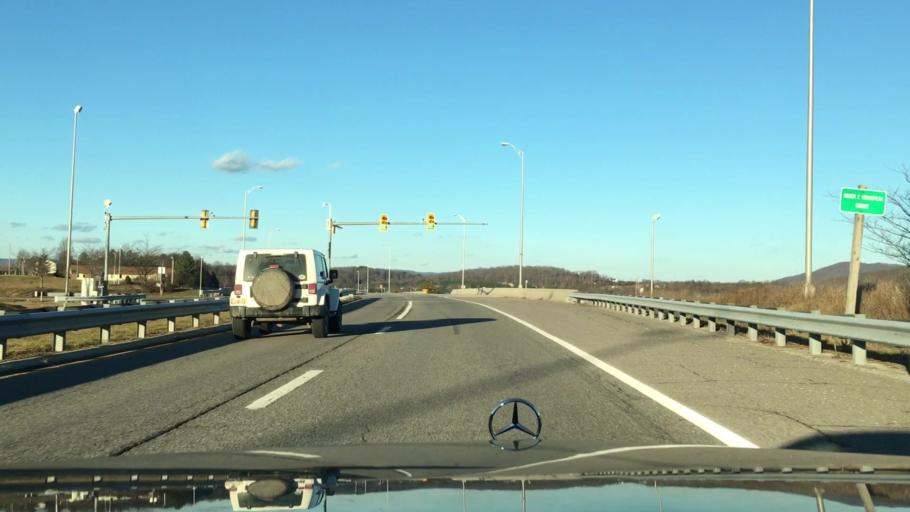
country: US
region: Virginia
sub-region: Montgomery County
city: Merrimac
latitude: 37.1911
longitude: -80.4041
